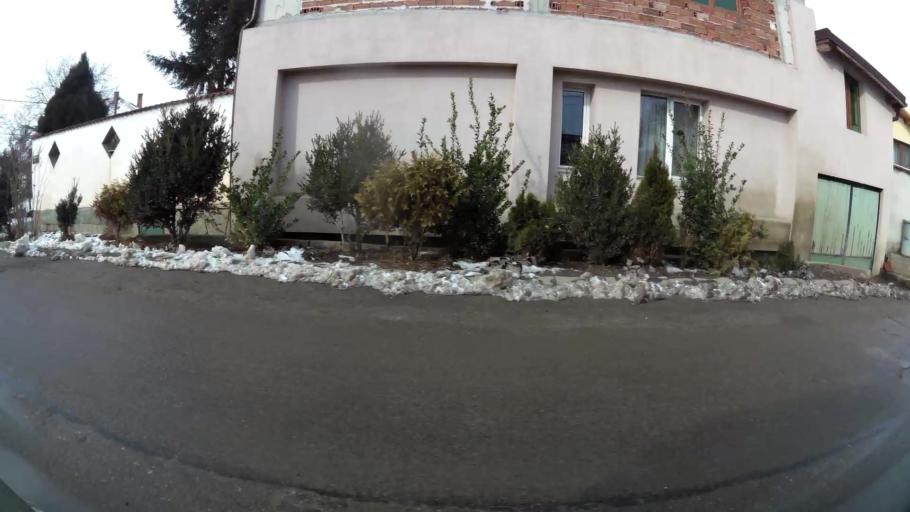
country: BG
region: Sofia-Capital
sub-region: Stolichna Obshtina
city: Sofia
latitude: 42.7118
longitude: 23.4197
